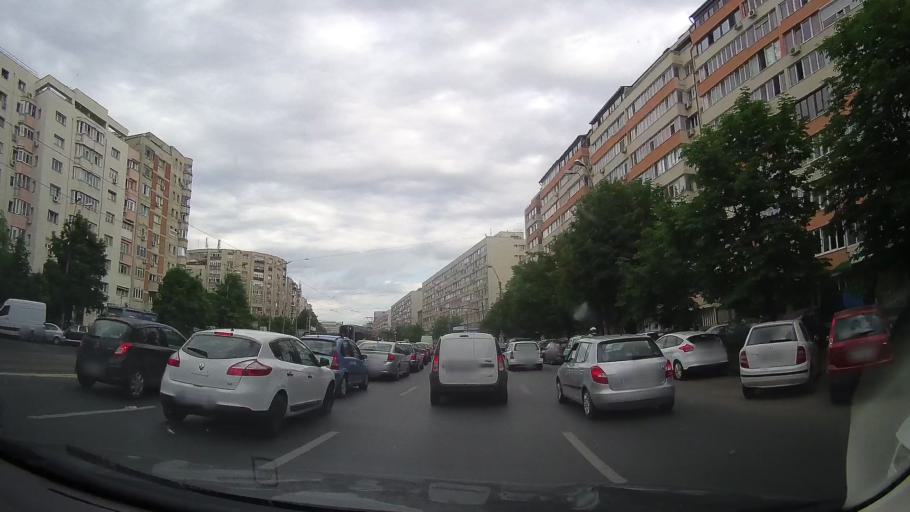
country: RO
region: Bucuresti
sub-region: Municipiul Bucuresti
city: Bucharest
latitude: 44.4366
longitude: 26.1369
